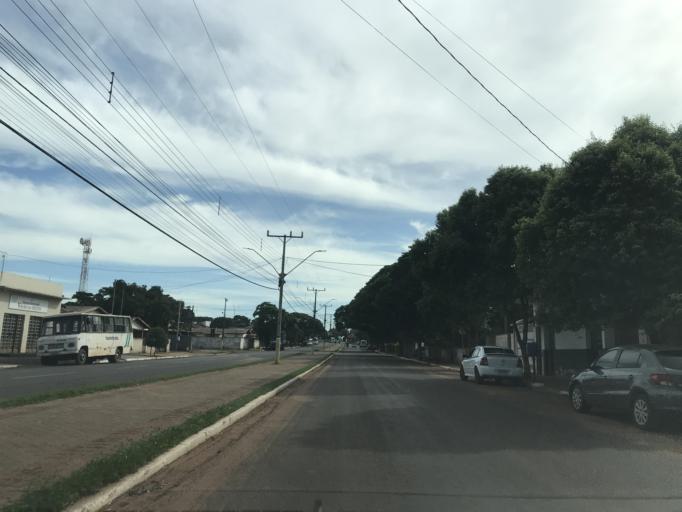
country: BR
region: Parana
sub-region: Paranavai
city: Nova Aurora
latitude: -22.9382
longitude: -52.6885
